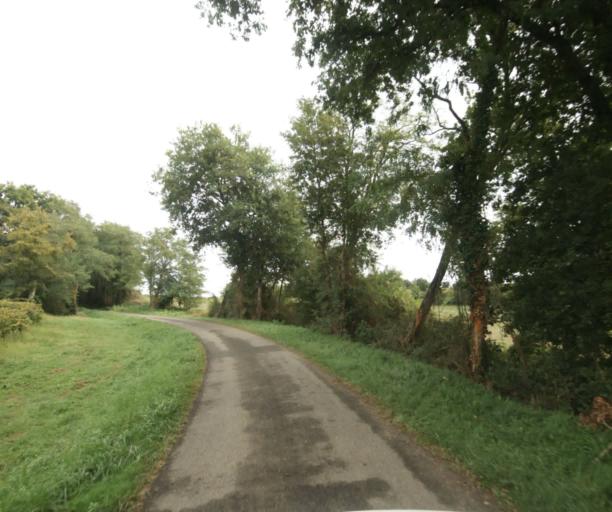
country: FR
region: Midi-Pyrenees
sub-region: Departement du Gers
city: Nogaro
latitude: 43.8291
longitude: -0.0727
